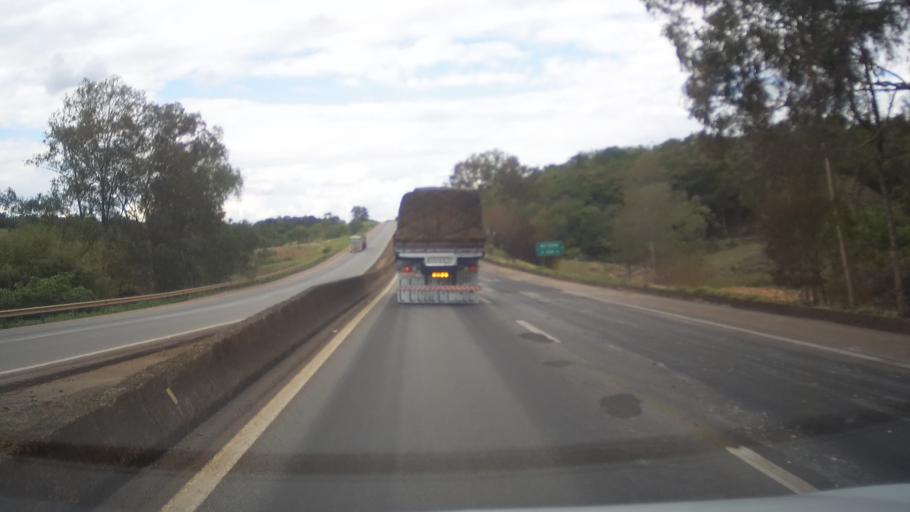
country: BR
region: Minas Gerais
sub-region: Itauna
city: Itauna
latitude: -20.3118
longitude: -44.4507
